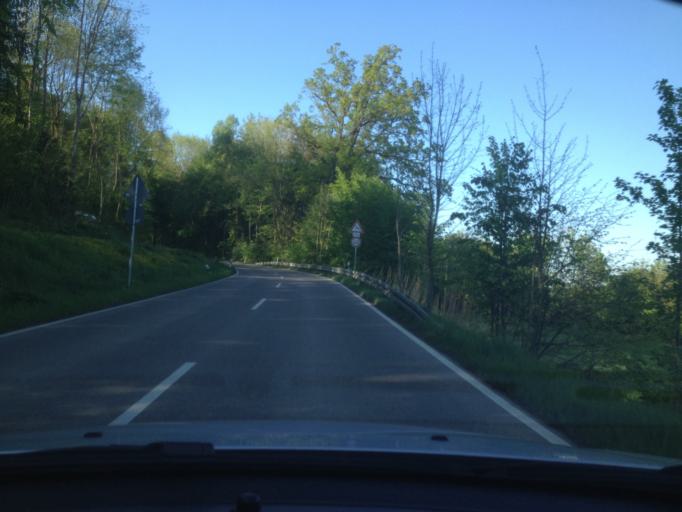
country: DE
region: Bavaria
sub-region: Swabia
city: Stadtbergen
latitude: 48.3278
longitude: 10.8235
